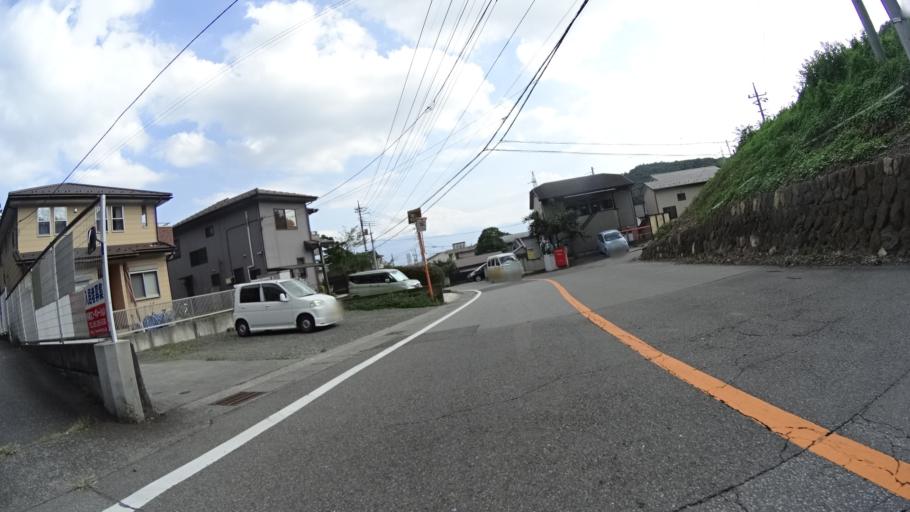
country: JP
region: Yamanashi
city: Kofu-shi
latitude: 35.6902
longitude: 138.5640
